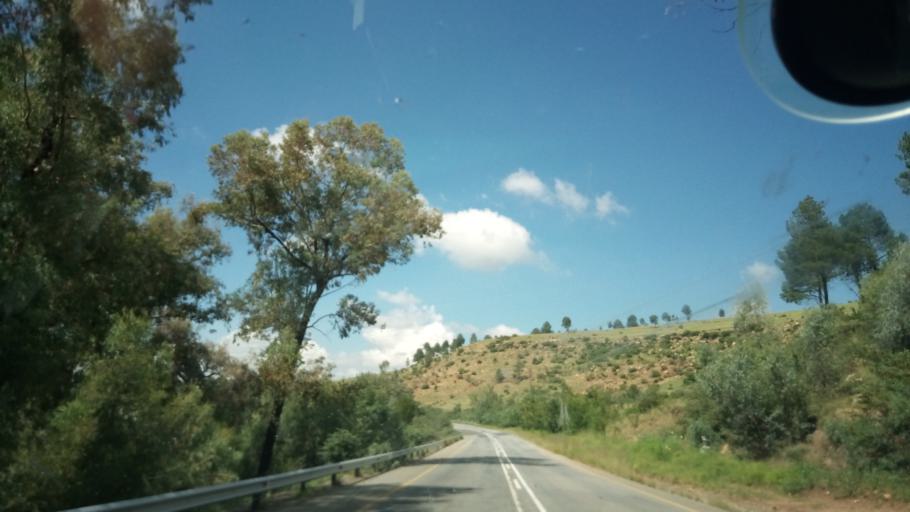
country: ZA
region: Orange Free State
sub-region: Thabo Mofutsanyana District Municipality
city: Ficksburg
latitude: -28.8766
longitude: 27.8660
